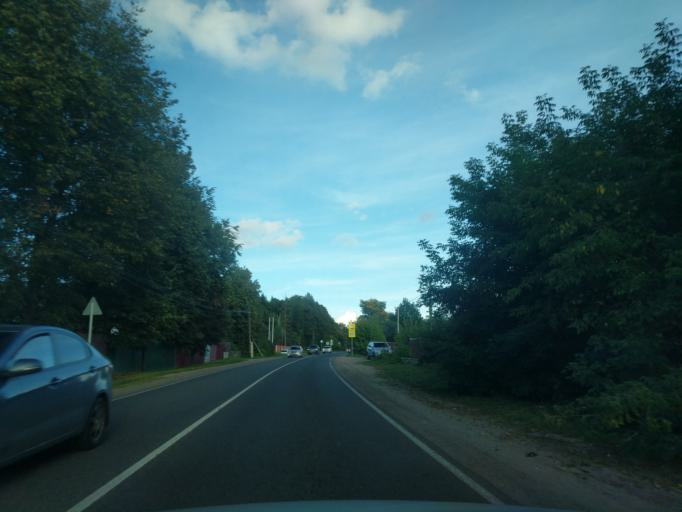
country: RU
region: Kirov
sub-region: Kirovo-Chepetskiy Rayon
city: Kirov
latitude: 58.6113
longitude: 49.7915
